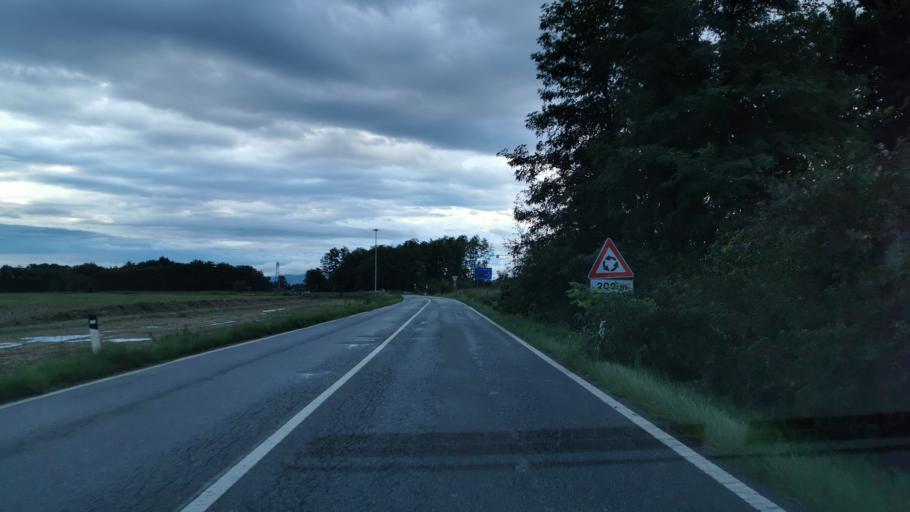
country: IT
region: Piedmont
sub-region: Provincia di Torino
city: Lombardore
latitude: 45.2300
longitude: 7.7525
